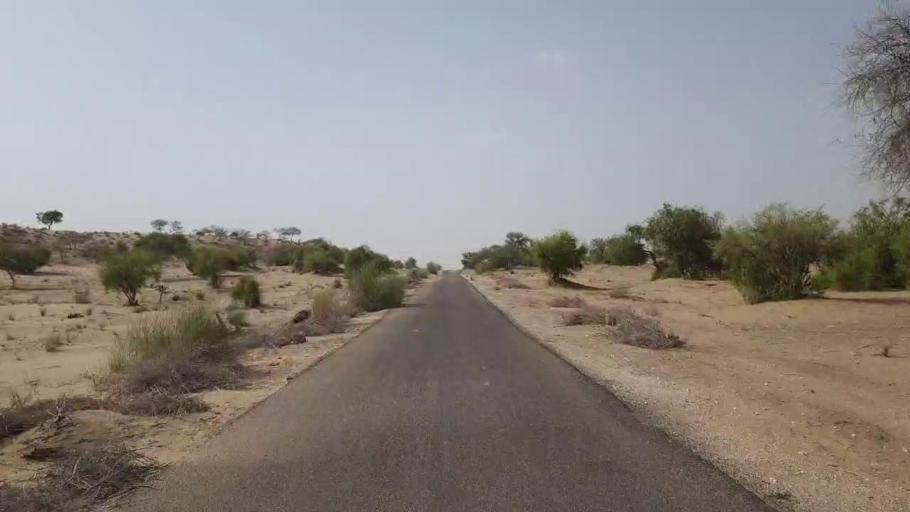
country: PK
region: Sindh
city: Mithi
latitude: 24.5857
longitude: 69.9228
